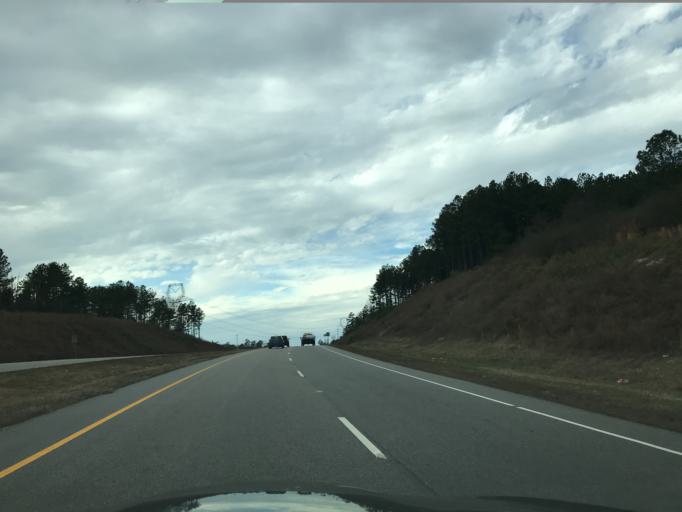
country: US
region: North Carolina
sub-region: Wake County
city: Rolesville
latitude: 35.8993
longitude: -78.4742
